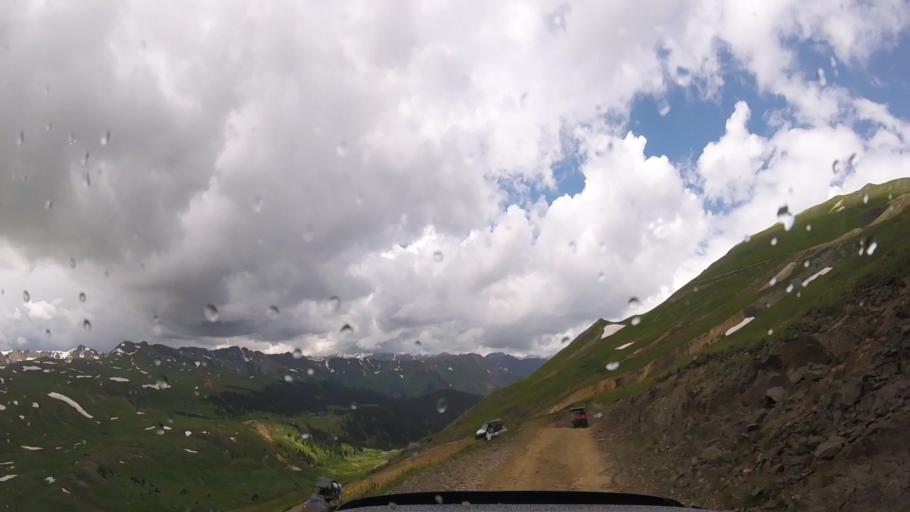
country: US
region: Colorado
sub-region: Ouray County
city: Ouray
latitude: 37.9635
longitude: -107.5778
